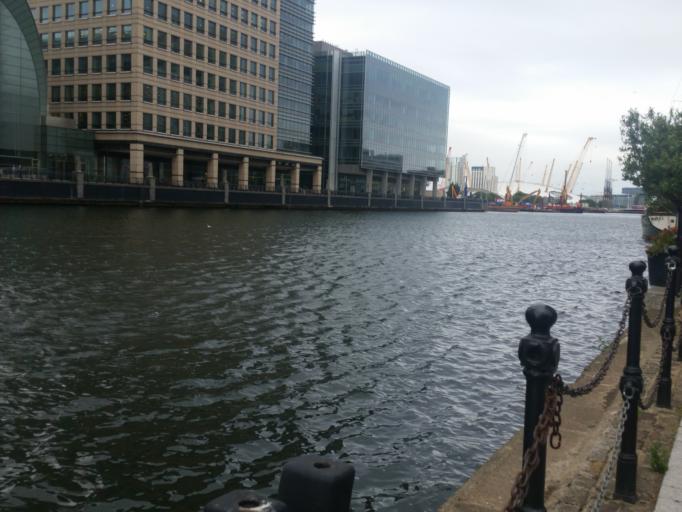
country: GB
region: England
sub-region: Greater London
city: Poplar
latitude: 51.5018
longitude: -0.0199
